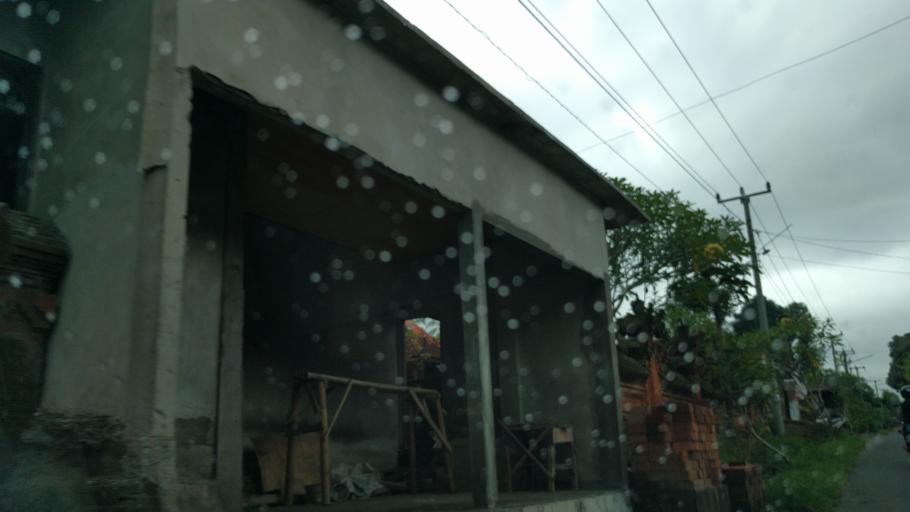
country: ID
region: Bali
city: Banjar Triwangsakeliki
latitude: -8.4530
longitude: 115.2612
